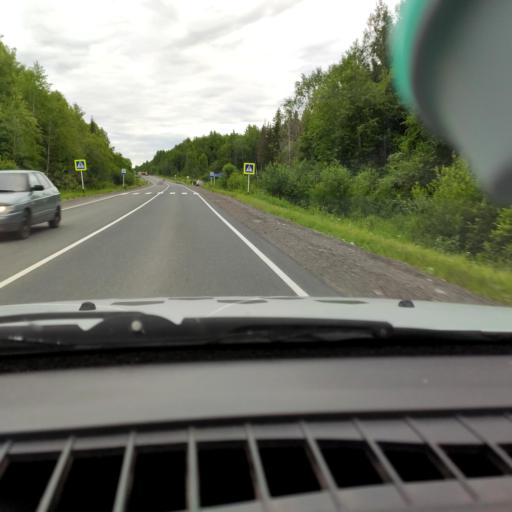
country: RU
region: Perm
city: Lys'va
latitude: 58.1902
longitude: 57.7951
